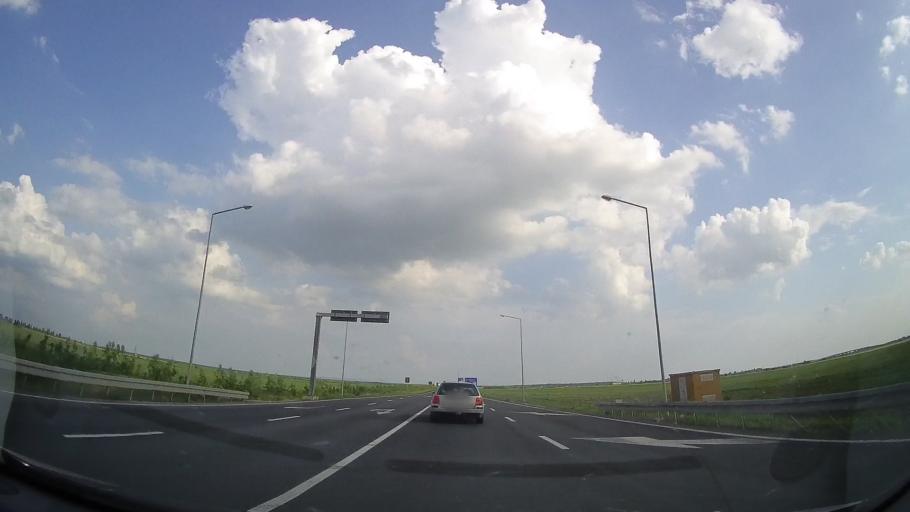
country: RO
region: Timis
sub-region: Comuna Remetea Mare
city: Remetea Mare
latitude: 45.8009
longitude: 21.4110
